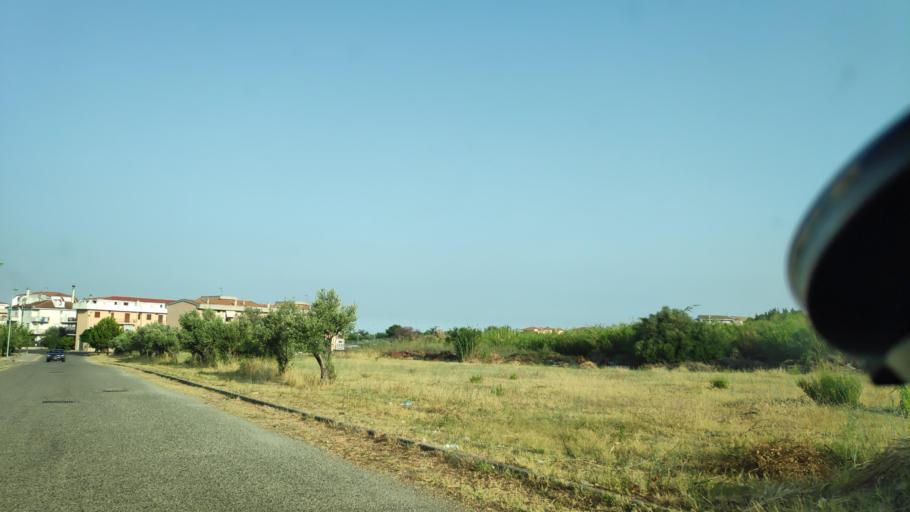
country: IT
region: Calabria
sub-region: Provincia di Catanzaro
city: Sant'Andrea Ionio Marina
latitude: 38.6185
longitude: 16.5503
